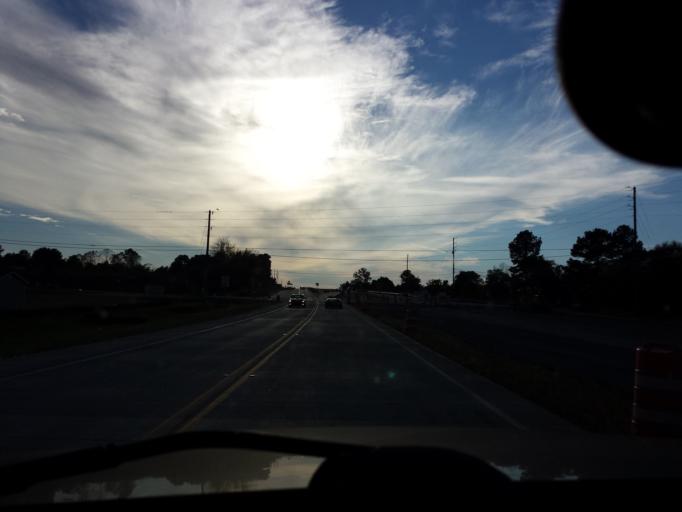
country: US
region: Georgia
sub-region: Bartow County
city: Euharlee
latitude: 34.1053
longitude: -84.9158
